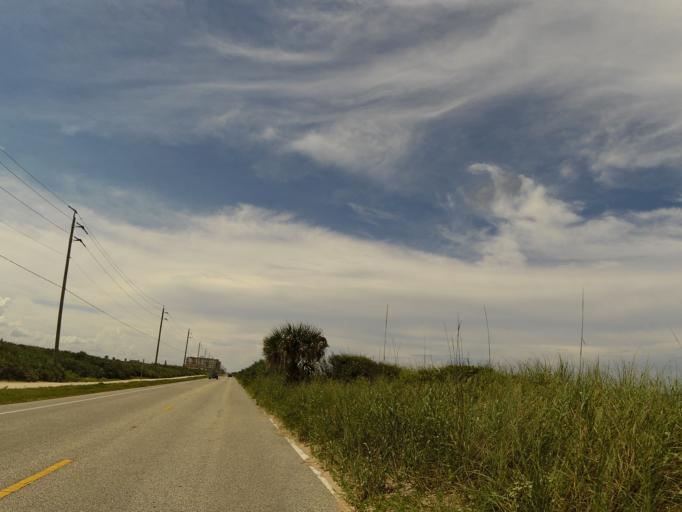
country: US
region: Florida
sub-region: Flagler County
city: Flagler Beach
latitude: 29.4228
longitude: -81.1007
